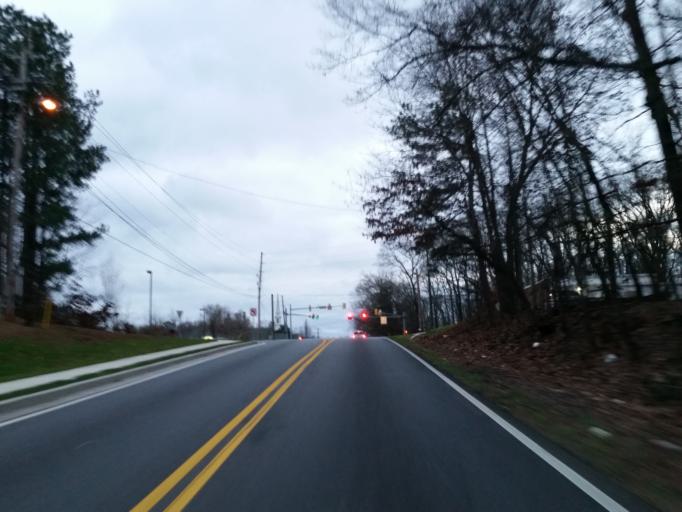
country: US
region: Georgia
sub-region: Cobb County
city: Mableton
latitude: 33.8661
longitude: -84.5773
